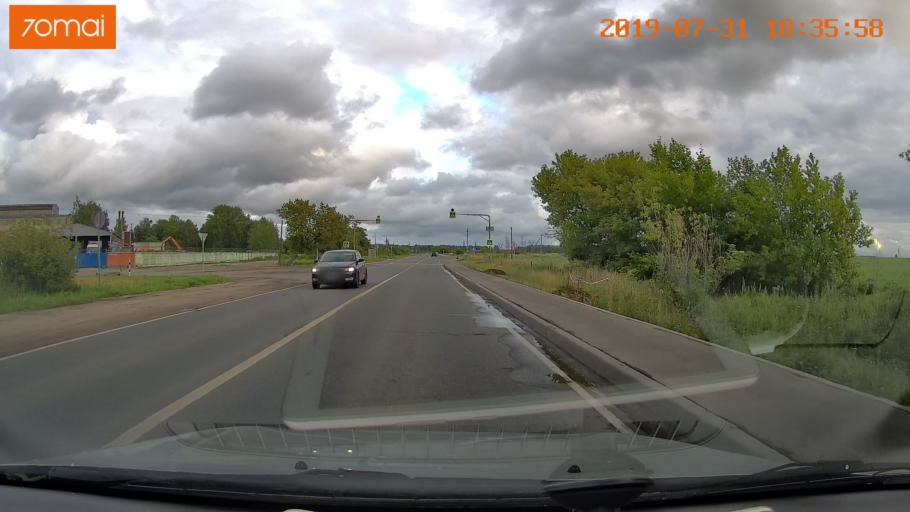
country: RU
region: Moskovskaya
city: Voskresensk
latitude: 55.2914
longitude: 38.6749
